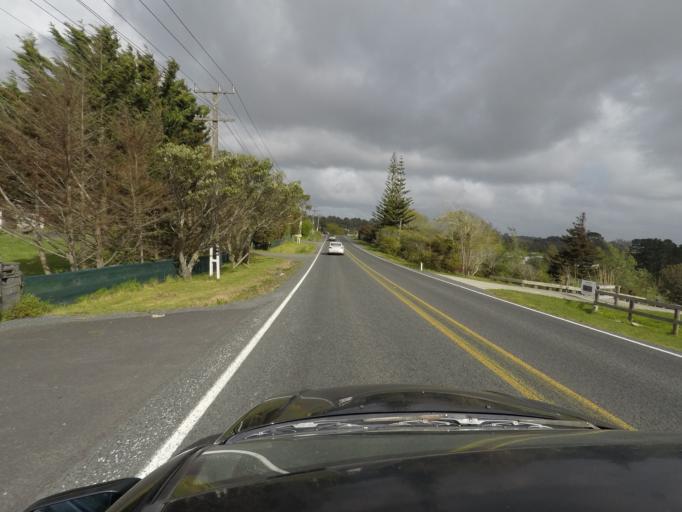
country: NZ
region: Auckland
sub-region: Auckland
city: Pakuranga
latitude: -36.9341
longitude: 174.9386
